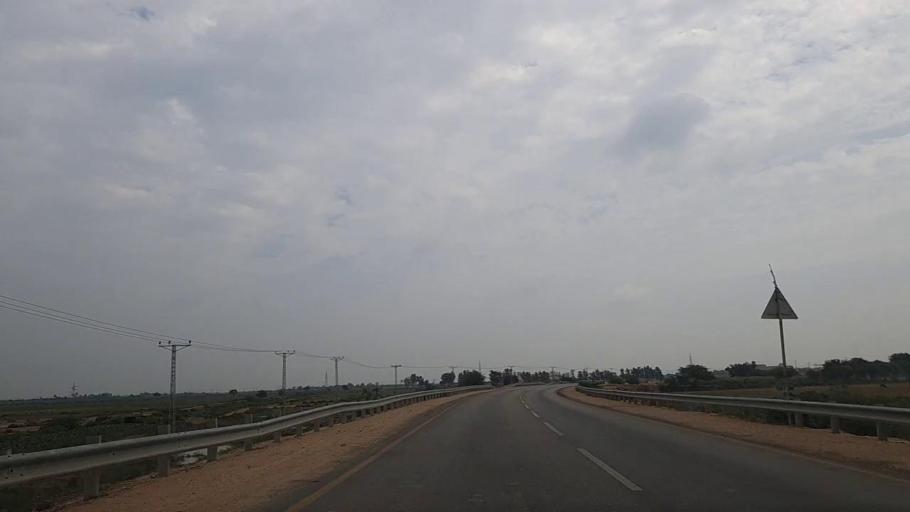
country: PK
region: Sindh
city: Daro Mehar
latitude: 24.6182
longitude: 68.0832
